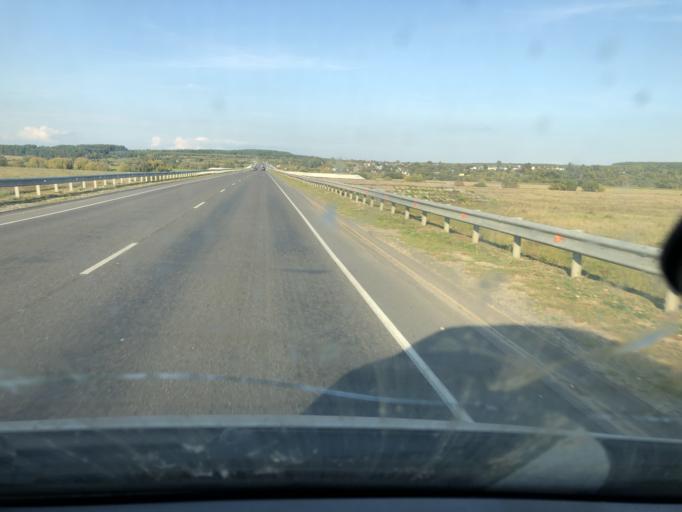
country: RU
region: Kaluga
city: Peremyshl'
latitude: 54.2868
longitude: 36.1628
